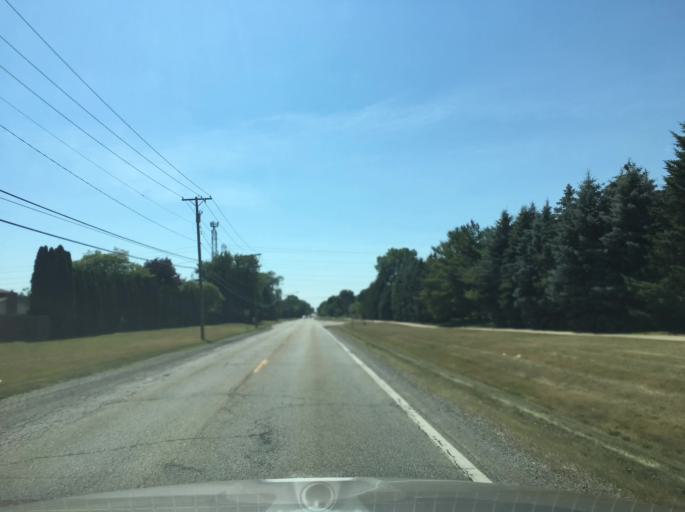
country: US
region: Michigan
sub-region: Macomb County
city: Utica
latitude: 42.6411
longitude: -82.9993
